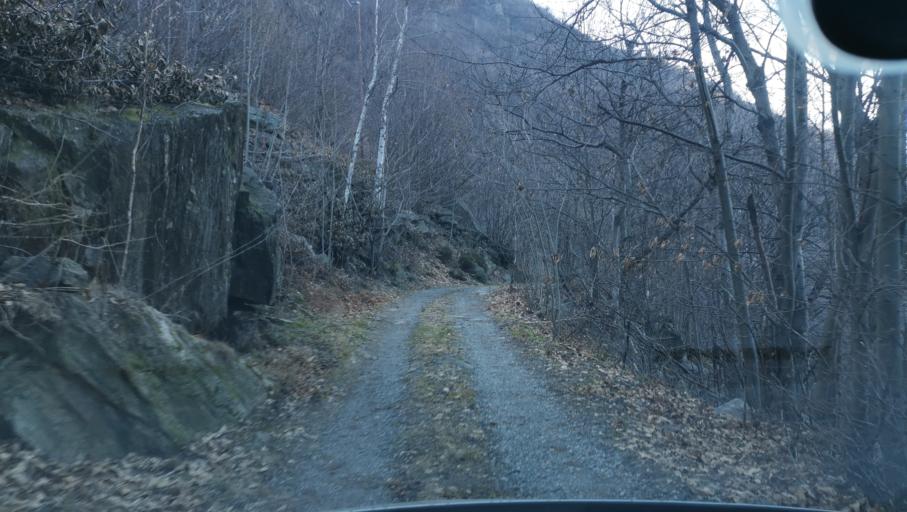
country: IT
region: Piedmont
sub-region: Provincia di Torino
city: Tavagnasco
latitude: 45.5383
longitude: 7.8201
